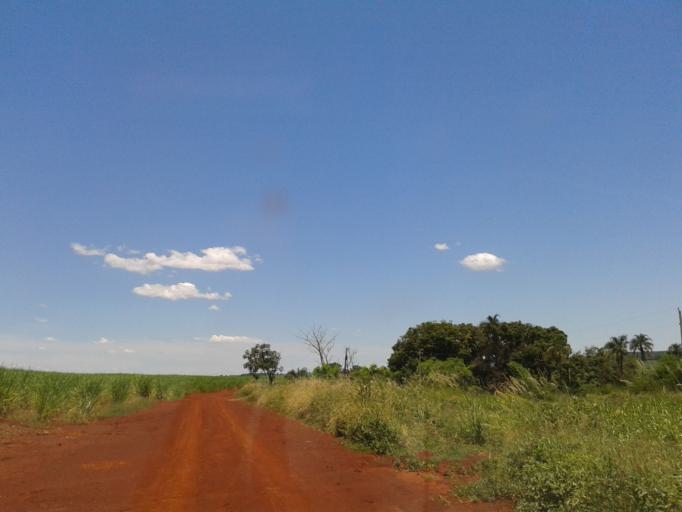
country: BR
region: Minas Gerais
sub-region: Centralina
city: Centralina
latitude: -18.6692
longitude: -49.2411
